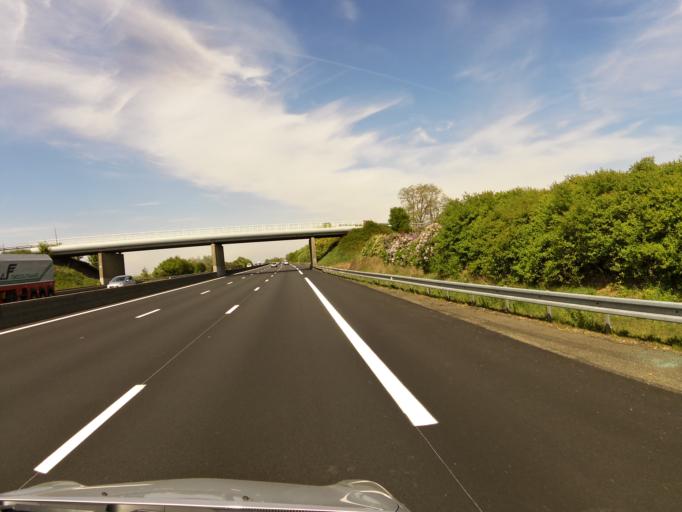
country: FR
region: Centre
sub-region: Departement d'Eure-et-Loir
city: Aunay-sous-Auneau
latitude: 48.3777
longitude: 1.8879
